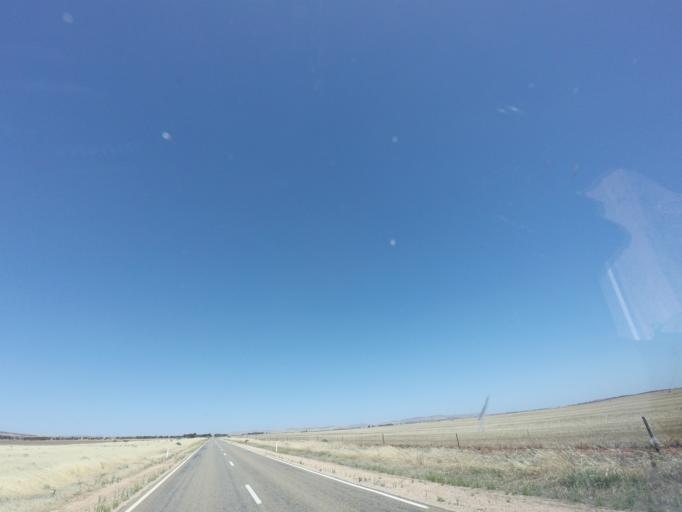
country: AU
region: South Australia
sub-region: Flinders Ranges
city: Quorn
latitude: -32.6937
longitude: 138.3591
